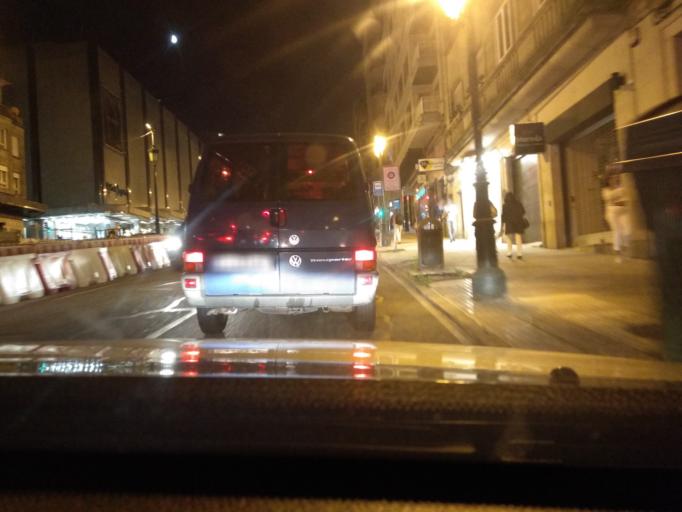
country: ES
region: Galicia
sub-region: Provincia de Pontevedra
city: Vigo
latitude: 42.2333
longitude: -8.7174
